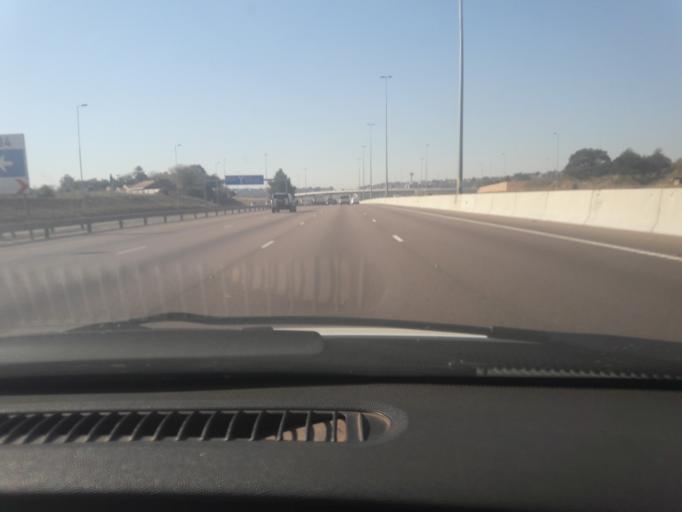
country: ZA
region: Gauteng
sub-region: City of Tshwane Metropolitan Municipality
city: Centurion
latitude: -25.8335
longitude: 28.2394
